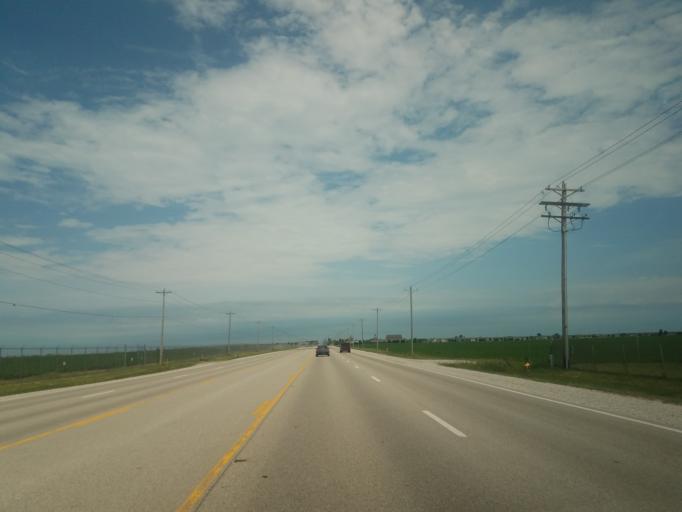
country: US
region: Illinois
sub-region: McLean County
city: Downs
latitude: 40.4787
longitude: -88.9023
